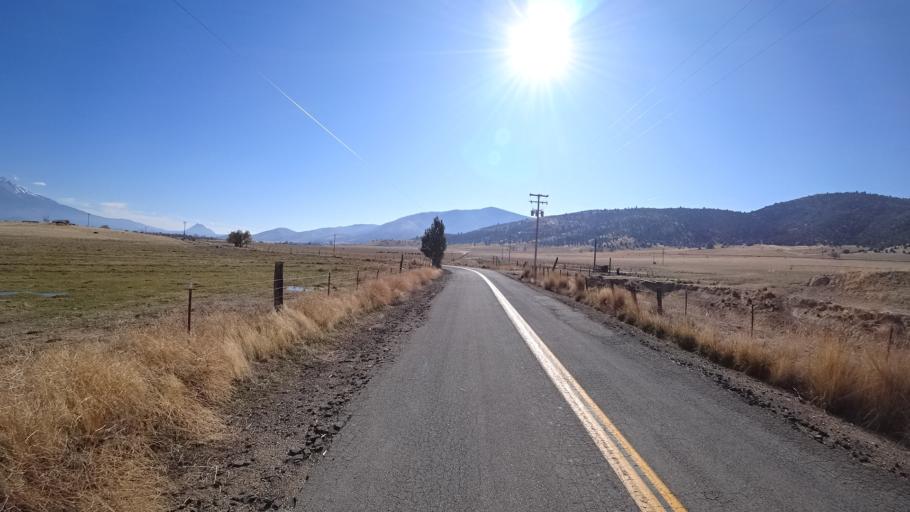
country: US
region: California
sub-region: Siskiyou County
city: Weed
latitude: 41.5294
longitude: -122.5349
